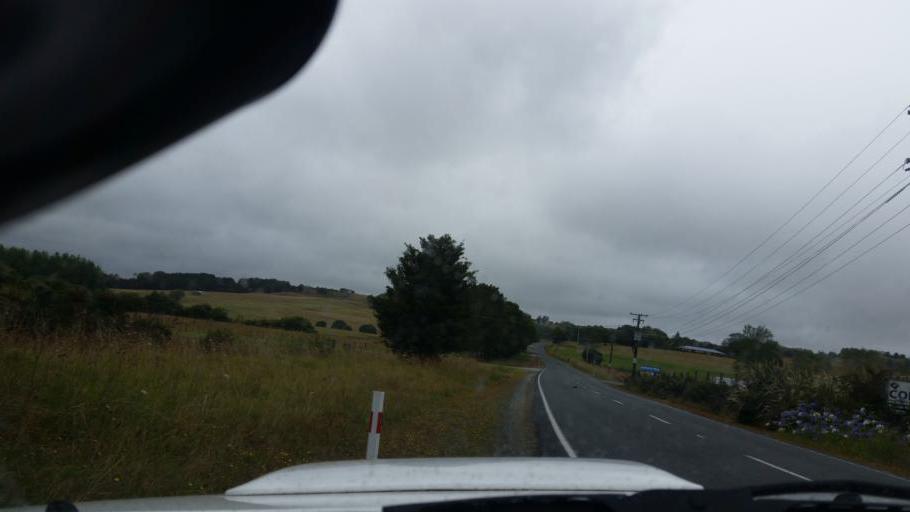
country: NZ
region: Auckland
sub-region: Auckland
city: Wellsford
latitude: -36.1385
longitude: 174.5145
